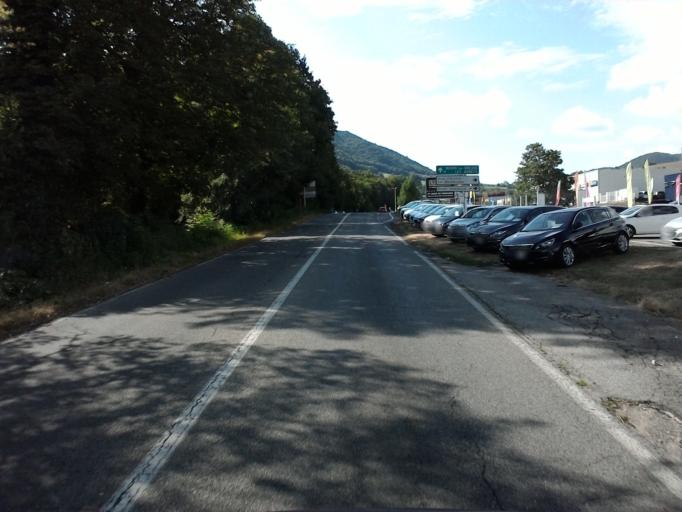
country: FR
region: Rhone-Alpes
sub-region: Departement de l'Isere
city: Voiron
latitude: 45.3812
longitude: 5.5792
